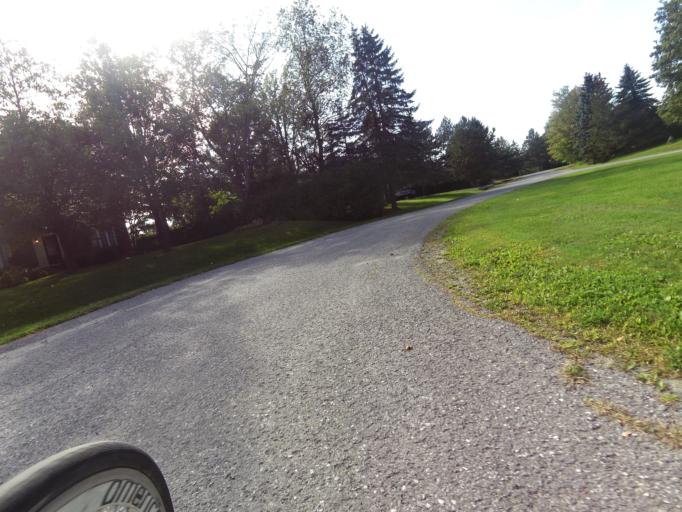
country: CA
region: Ontario
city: Bells Corners
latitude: 45.2672
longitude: -75.7152
